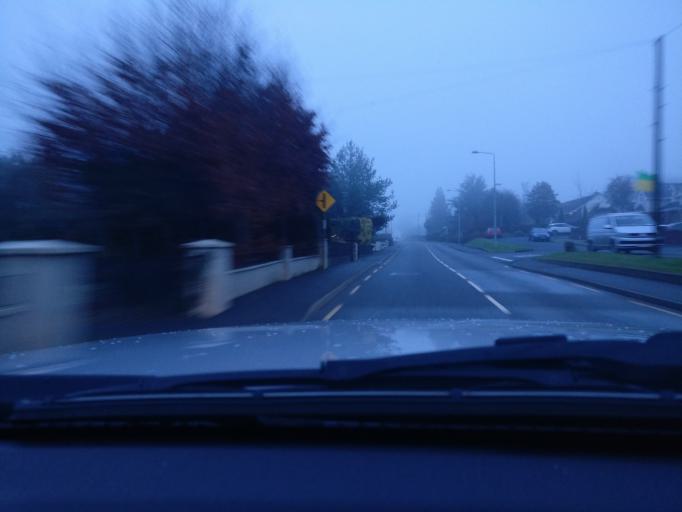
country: IE
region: Leinster
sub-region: An Mhi
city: Athboy
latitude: 53.6265
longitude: -6.9078
